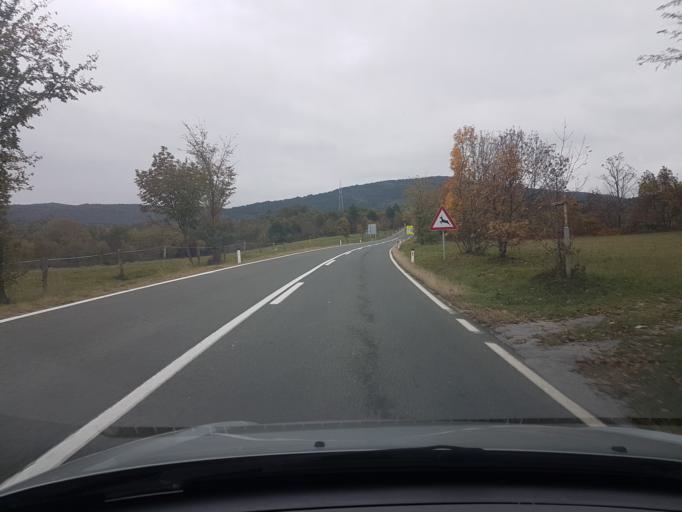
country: SI
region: Divaca
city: Divaca
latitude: 45.7398
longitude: 13.9336
